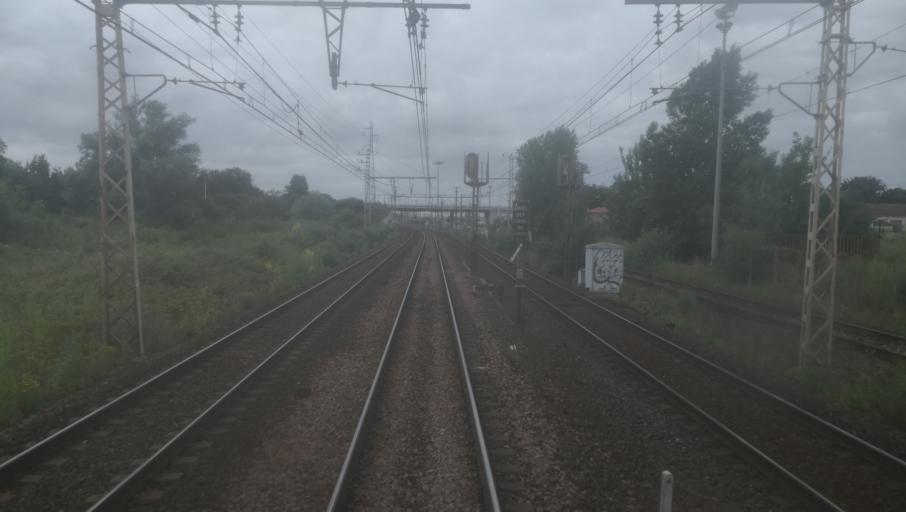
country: FR
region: Midi-Pyrenees
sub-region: Departement de la Haute-Garonne
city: Fenouillet
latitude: 43.6826
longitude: 1.4025
